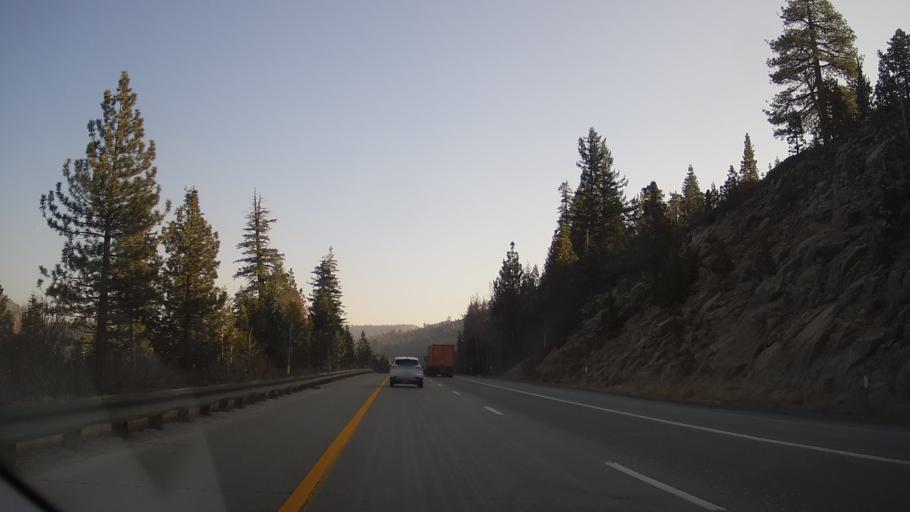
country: US
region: California
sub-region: Sierra County
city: Downieville
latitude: 39.3246
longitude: -120.5702
